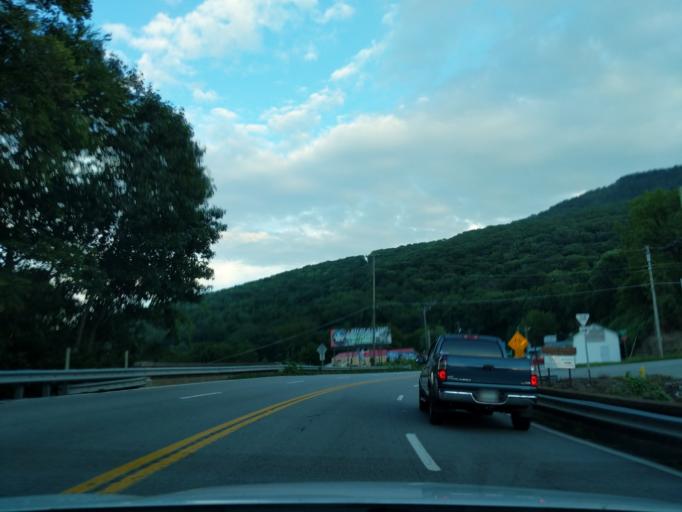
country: US
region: Tennessee
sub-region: Hamilton County
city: Lookout Mountain
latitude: 35.0211
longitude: -85.3542
